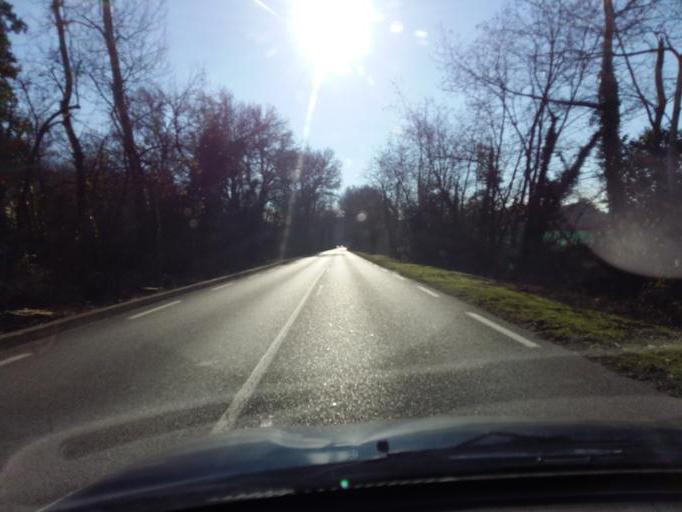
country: FR
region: Languedoc-Roussillon
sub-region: Departement du Gard
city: Roquemaure
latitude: 44.0606
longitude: 4.7708
